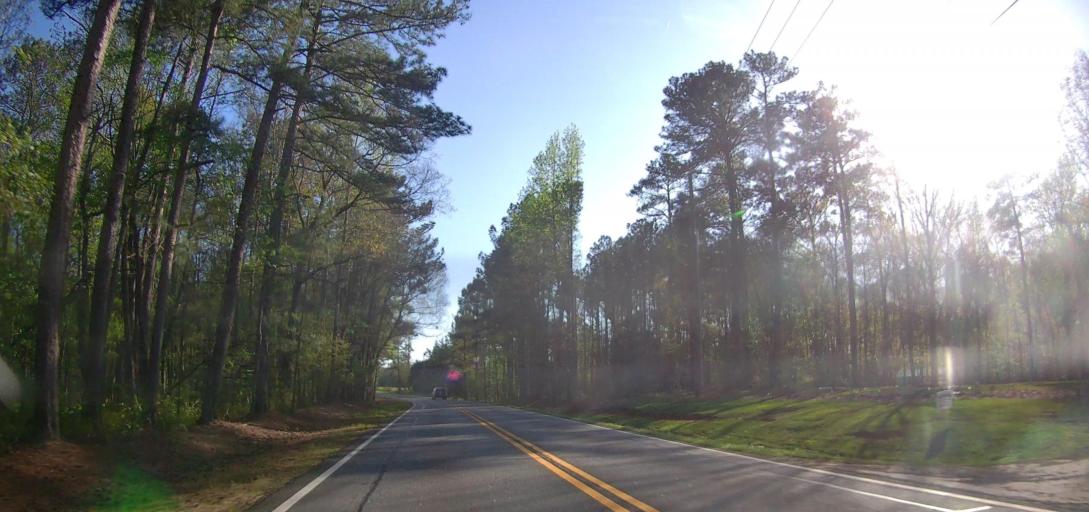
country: US
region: Georgia
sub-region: Monroe County
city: Forsyth
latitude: 33.0876
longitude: -83.9504
